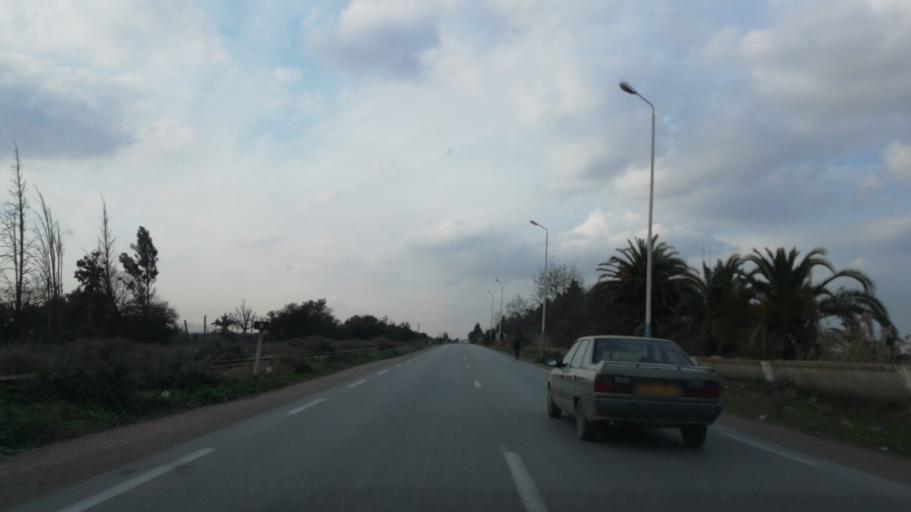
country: DZ
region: Mascara
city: Sig
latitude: 35.6571
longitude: 0.0132
